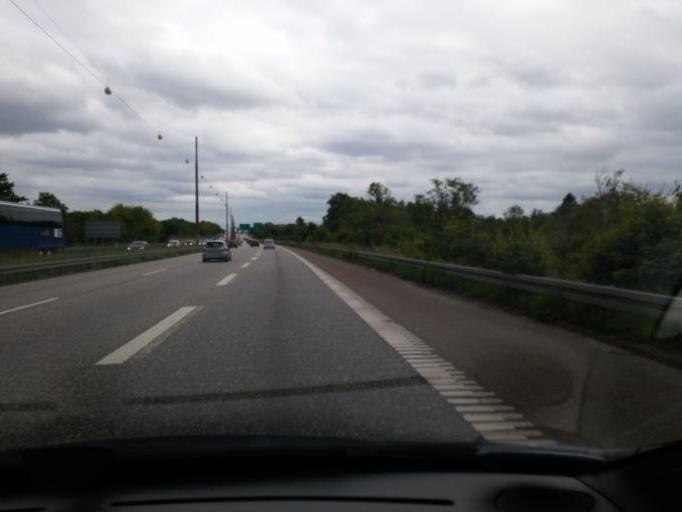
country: DK
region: Capital Region
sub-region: Herlev Kommune
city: Herlev
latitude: 55.7522
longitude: 12.4469
